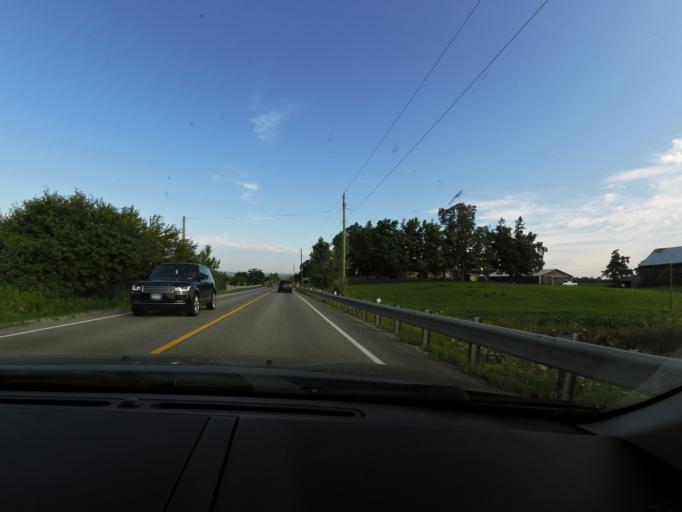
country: CA
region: Ontario
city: Brampton
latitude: 43.8202
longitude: -79.8705
